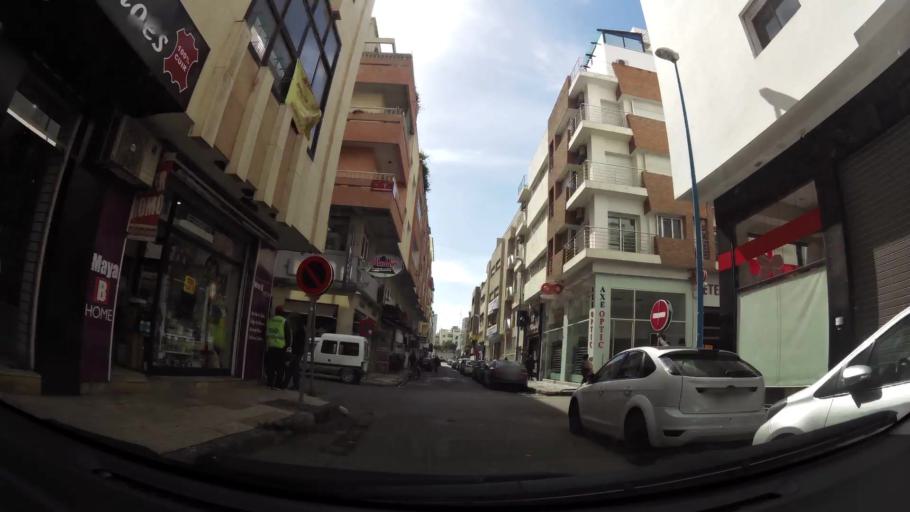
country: MA
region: Grand Casablanca
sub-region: Casablanca
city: Casablanca
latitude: 33.5847
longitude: -7.6334
